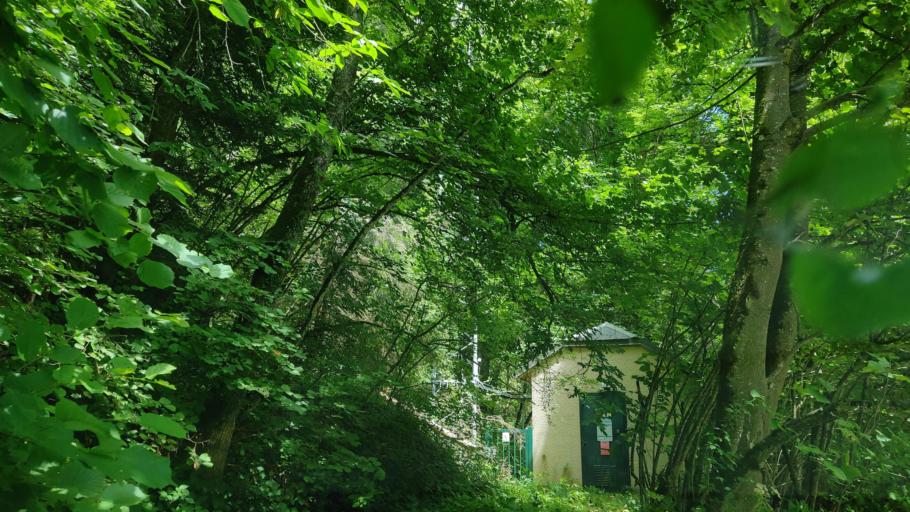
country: FR
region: Rhone-Alpes
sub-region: Departement de la Savoie
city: Aiton
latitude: 45.5122
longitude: 6.2794
